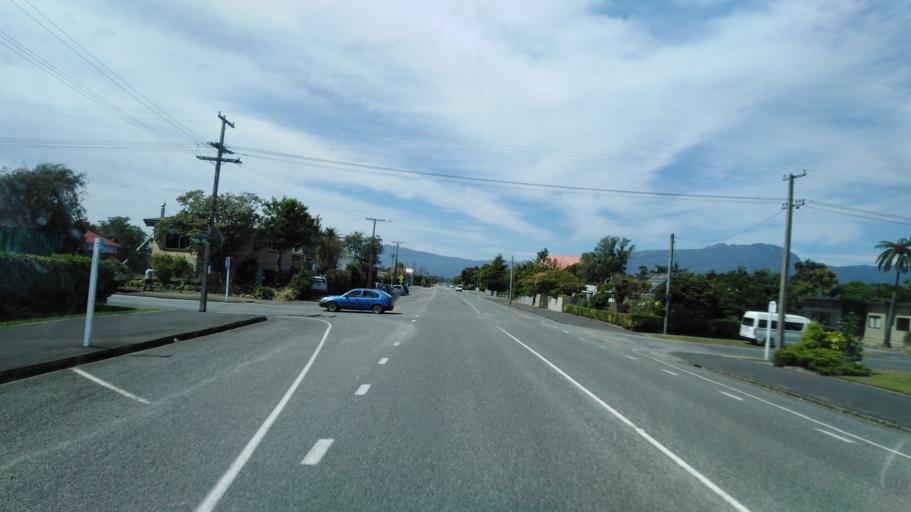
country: NZ
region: West Coast
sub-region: Buller District
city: Westport
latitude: -41.7549
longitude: 171.6026
